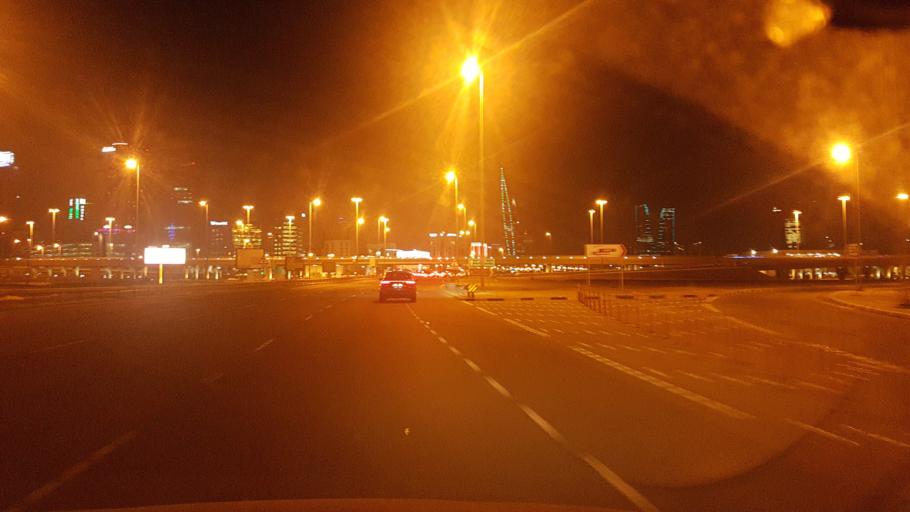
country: BH
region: Muharraq
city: Al Muharraq
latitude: 26.2492
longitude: 50.5917
